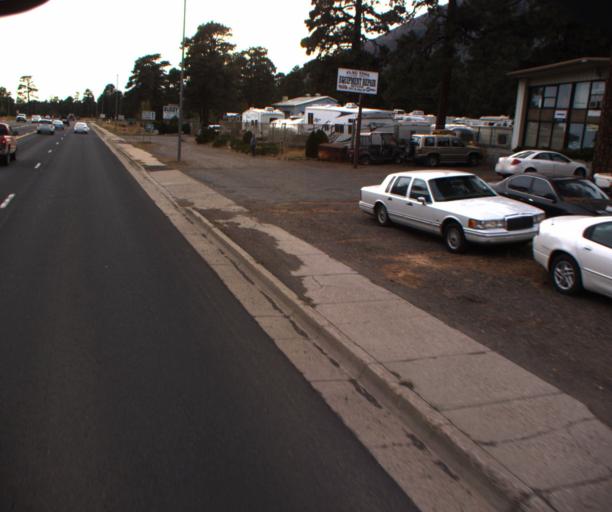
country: US
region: Arizona
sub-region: Coconino County
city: Flagstaff
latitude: 35.2406
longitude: -111.5699
